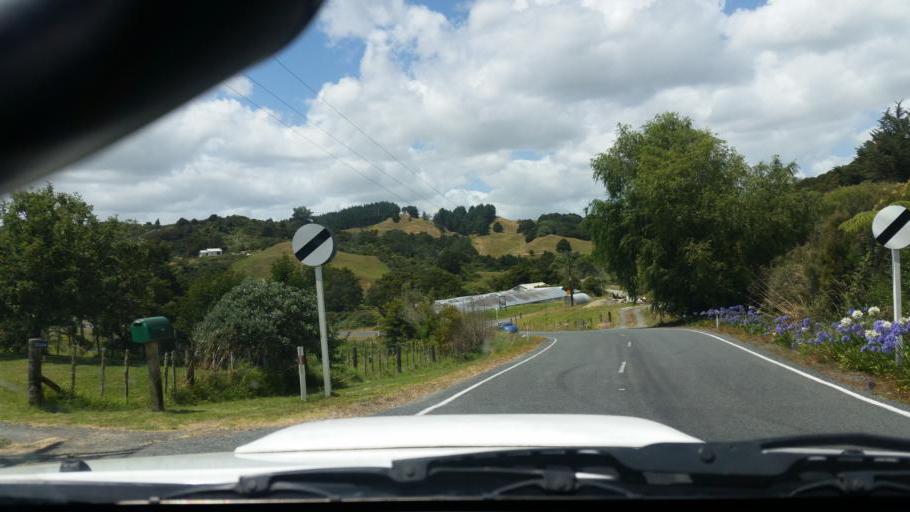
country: NZ
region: Northland
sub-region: Whangarei
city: Ruakaka
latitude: -36.0964
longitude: 174.2416
